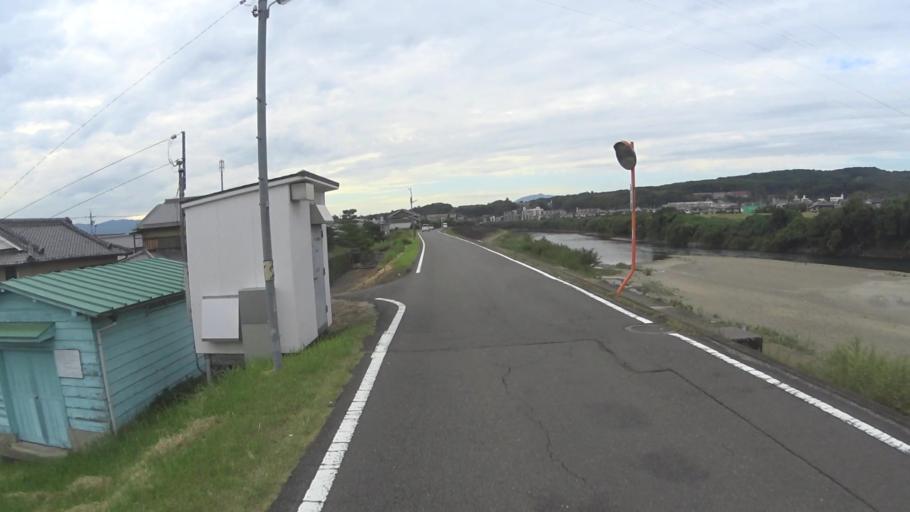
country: JP
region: Kyoto
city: Uji
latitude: 34.9235
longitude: 135.7839
